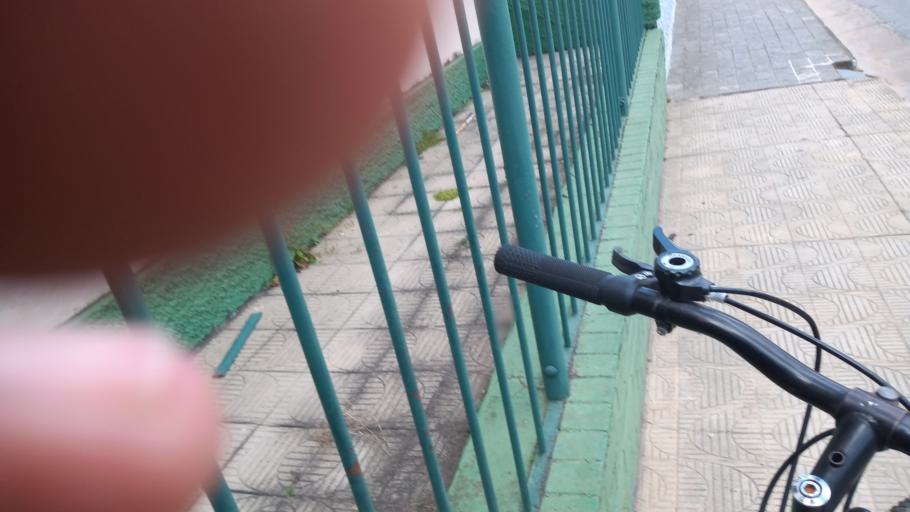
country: BR
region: Minas Gerais
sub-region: Sao Joao Del Rei
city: Sao Joao del Rei
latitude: -21.1229
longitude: -44.2487
